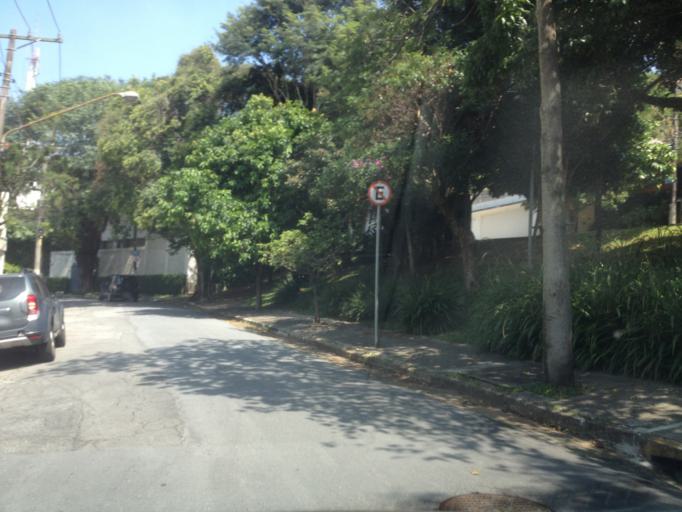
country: BR
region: Sao Paulo
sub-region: Sao Paulo
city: Sao Paulo
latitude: -23.5453
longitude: -46.6786
